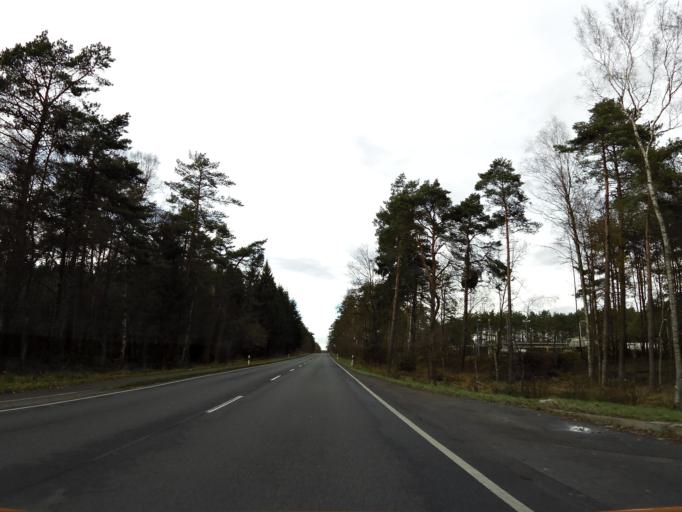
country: DE
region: Lower Saxony
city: Munster
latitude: 52.9612
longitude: 10.1151
